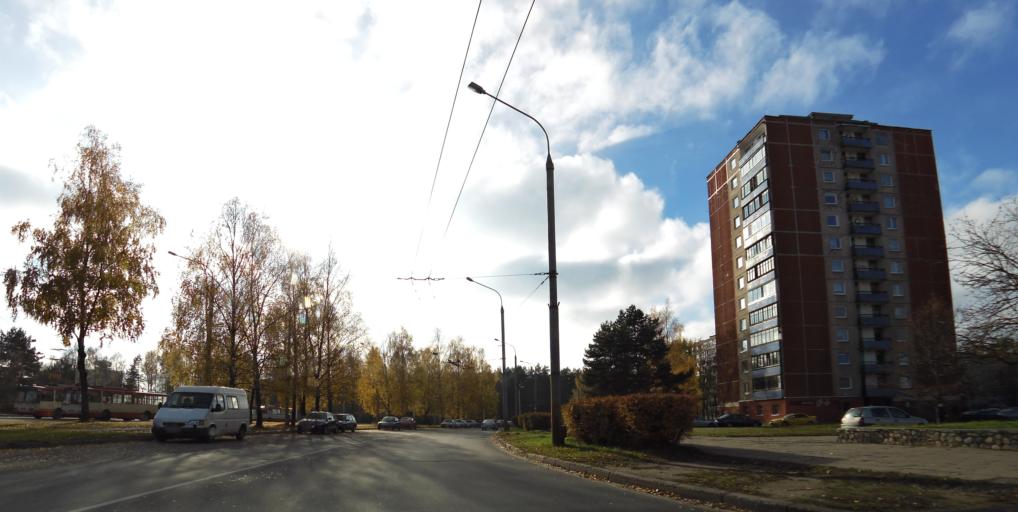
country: LT
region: Vilnius County
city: Lazdynai
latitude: 54.6848
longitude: 25.2056
